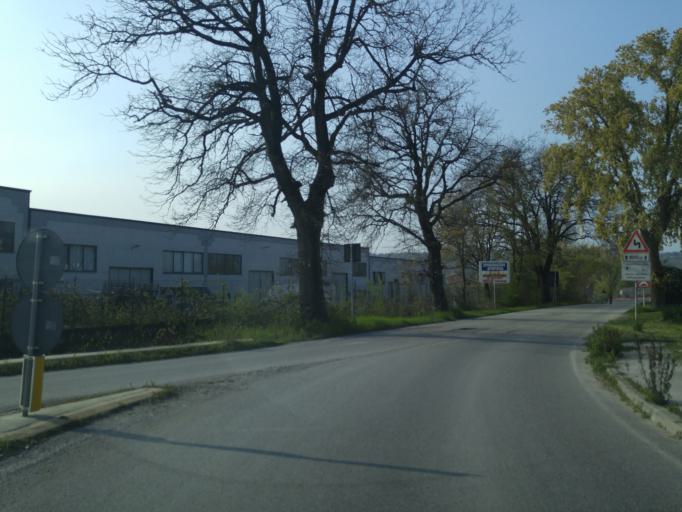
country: IT
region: The Marches
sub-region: Provincia di Pesaro e Urbino
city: Tavernelle
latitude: 43.7188
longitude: 12.8984
